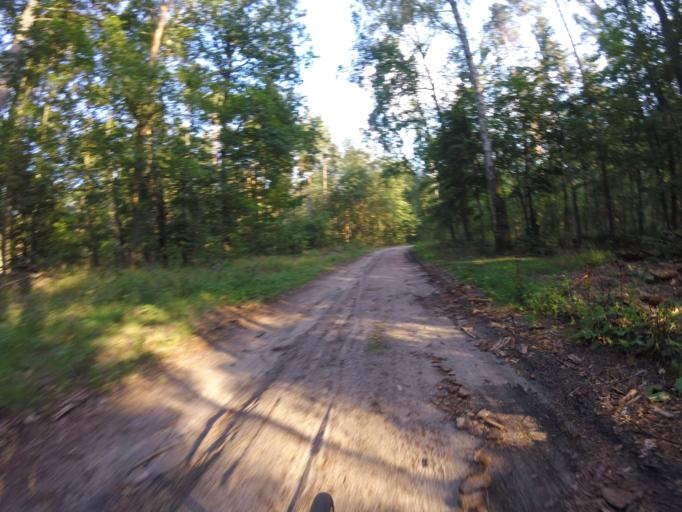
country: DE
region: Brandenburg
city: Petershagen
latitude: 52.5688
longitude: 13.8233
